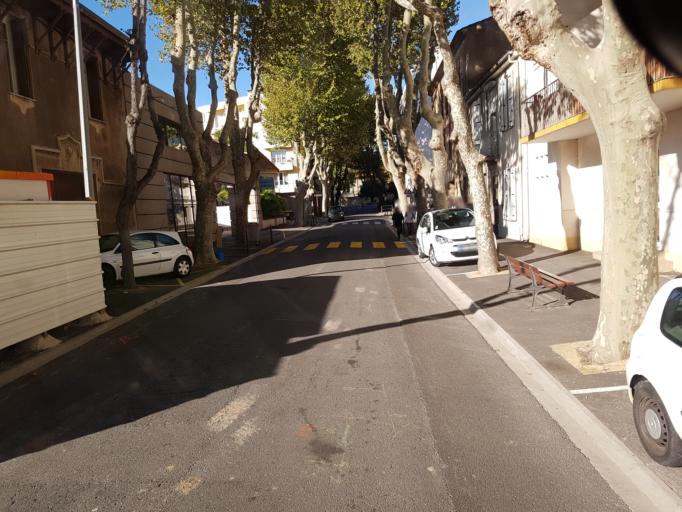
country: FR
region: Languedoc-Roussillon
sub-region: Departement de l'Aude
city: Narbonne
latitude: 43.1787
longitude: 3.0034
